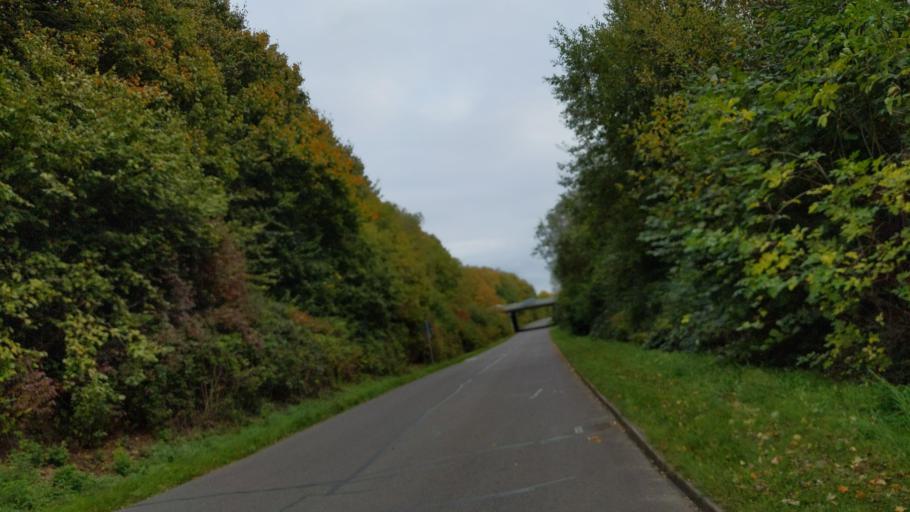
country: DE
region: Schleswig-Holstein
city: Sierksdorf
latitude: 54.0672
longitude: 10.7510
